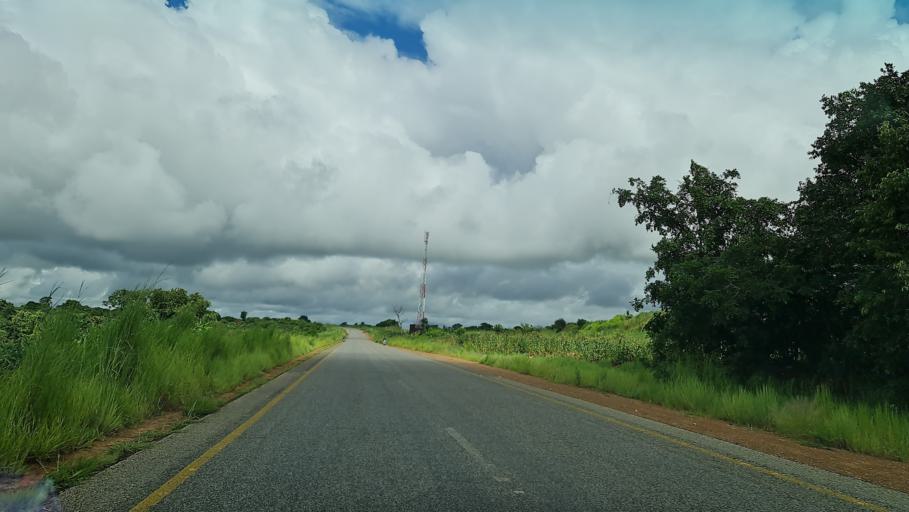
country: MZ
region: Nampula
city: Nampula
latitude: -15.0311
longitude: 38.4426
